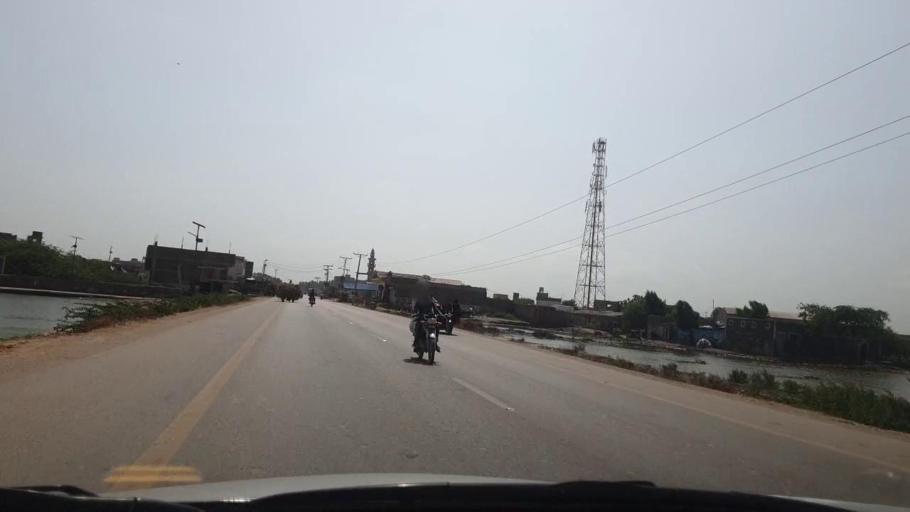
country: PK
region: Sindh
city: Matli
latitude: 25.0360
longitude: 68.6531
